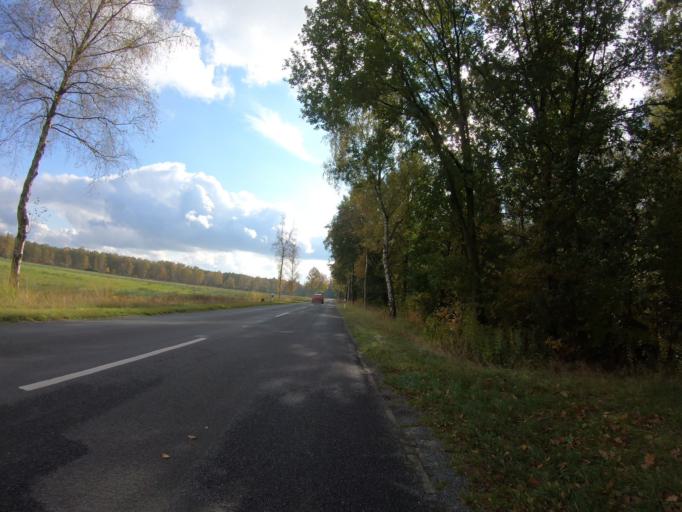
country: DE
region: Lower Saxony
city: Schoneworde
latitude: 52.5930
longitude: 10.6428
